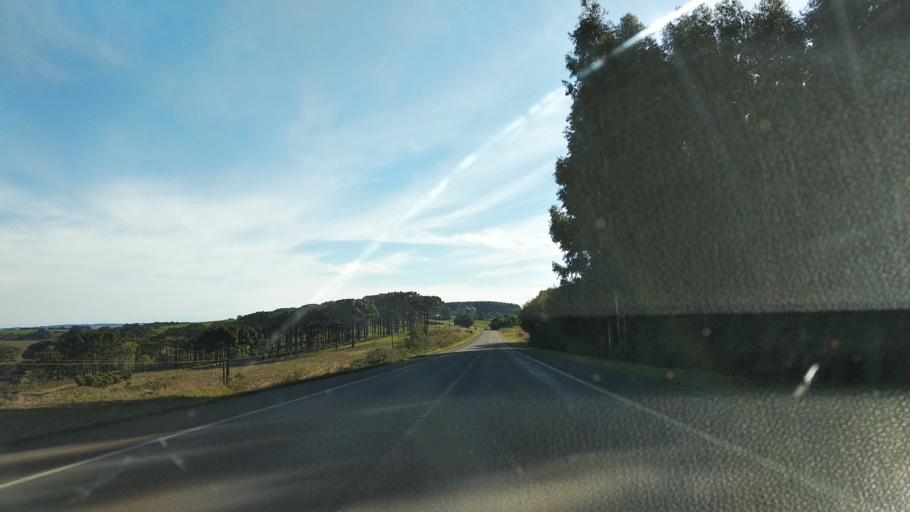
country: BR
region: Santa Catarina
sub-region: Celso Ramos
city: Celso Ramos
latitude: -27.5270
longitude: -51.3685
